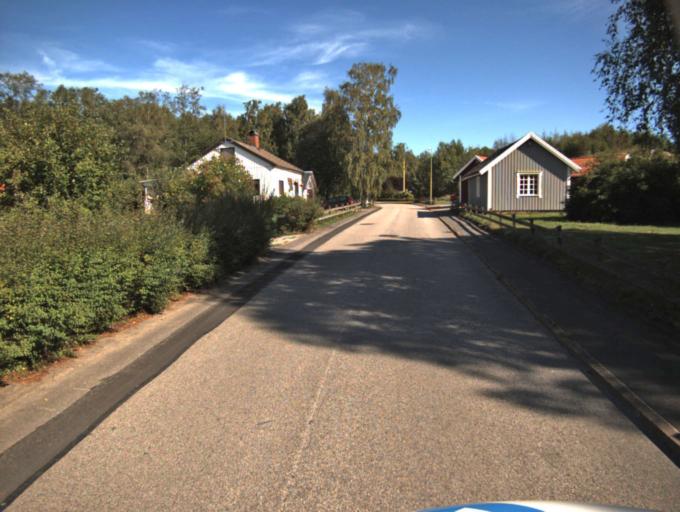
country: SE
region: Vaestra Goetaland
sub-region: Ulricehamns Kommun
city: Ulricehamn
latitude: 57.9005
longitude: 13.4589
